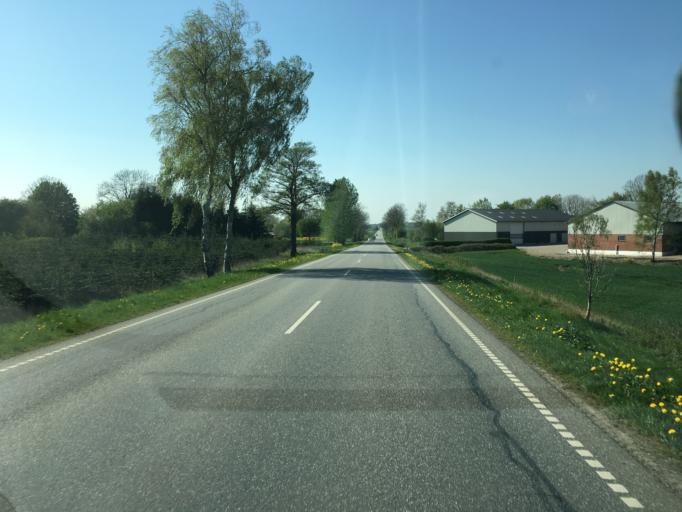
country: DK
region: South Denmark
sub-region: Haderslev Kommune
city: Vojens
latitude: 55.3073
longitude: 9.3496
